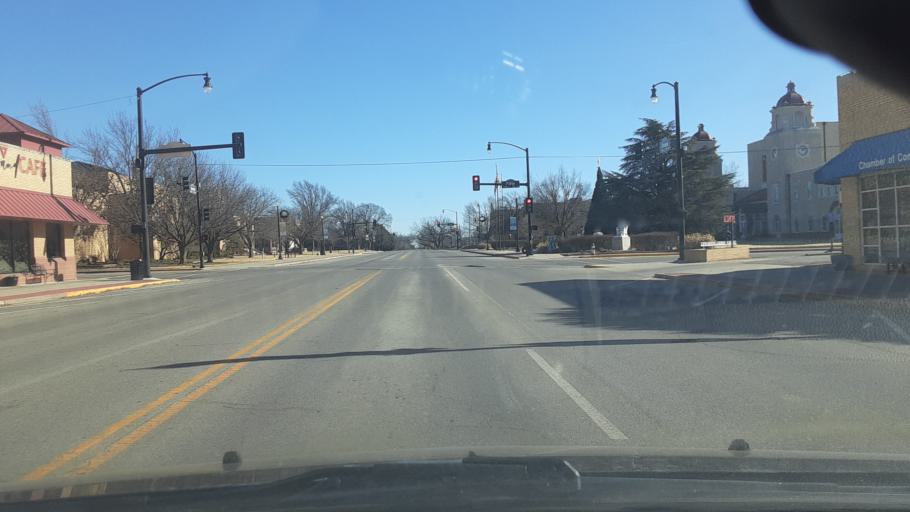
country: US
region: Oklahoma
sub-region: Kay County
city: Ponca City
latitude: 36.7036
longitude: -97.0792
